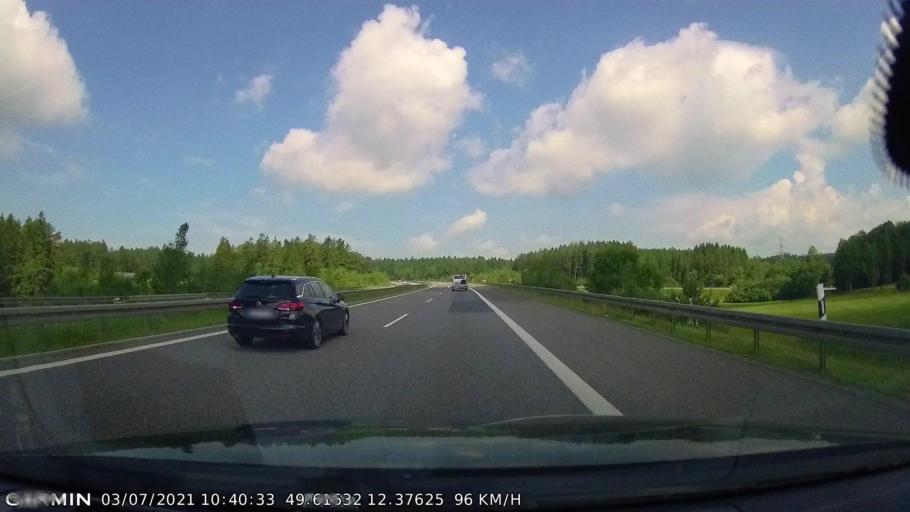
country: DE
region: Bavaria
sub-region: Upper Palatinate
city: Vohenstrauss
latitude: 49.6153
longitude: 12.3763
